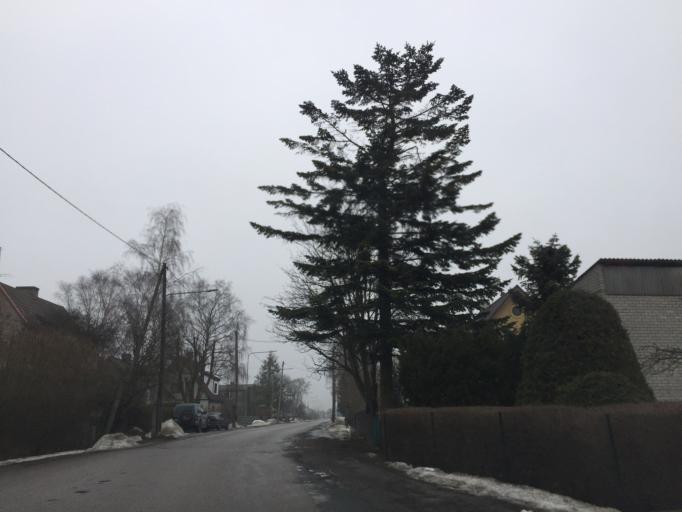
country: EE
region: Saare
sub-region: Kuressaare linn
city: Kuressaare
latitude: 58.2481
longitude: 22.4940
